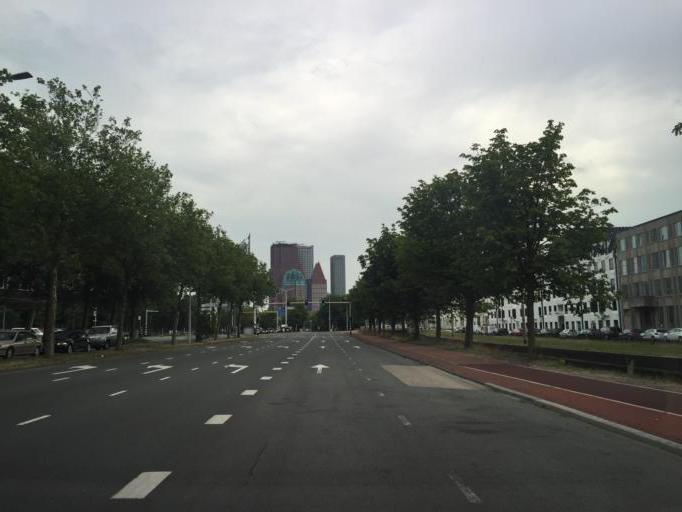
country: NL
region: South Holland
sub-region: Gemeente Den Haag
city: The Hague
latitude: 52.0869
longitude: 4.3149
